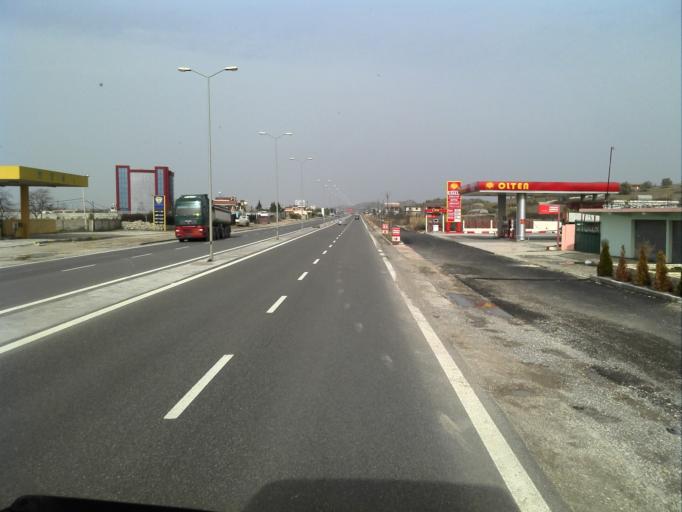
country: AL
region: Tirane
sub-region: Rrethi i Kavajes
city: Luzi i Vogel
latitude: 41.1383
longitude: 19.5935
